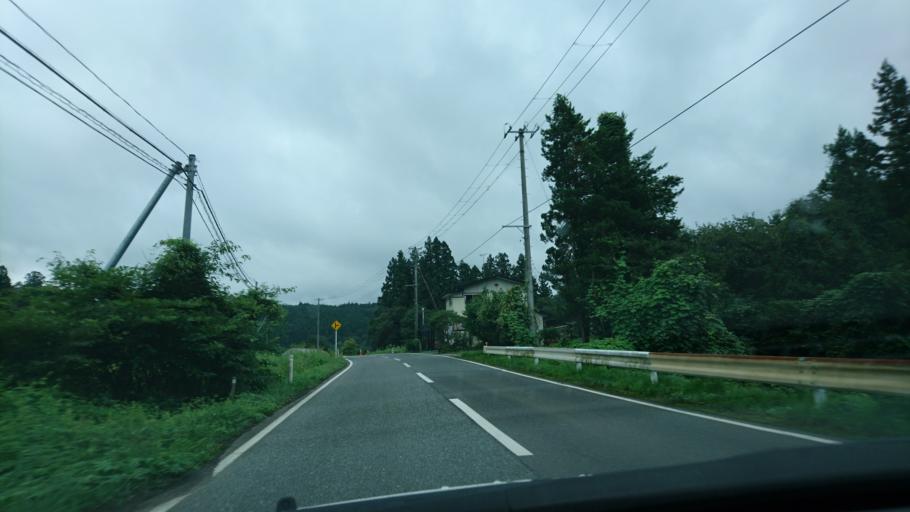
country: JP
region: Iwate
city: Ichinoseki
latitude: 38.9096
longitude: 141.0611
